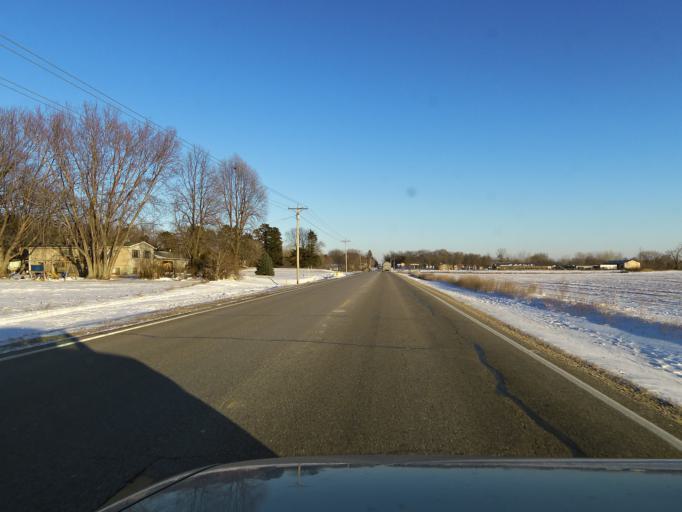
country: US
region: Minnesota
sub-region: Rice County
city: Northfield
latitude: 44.5436
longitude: -93.1622
